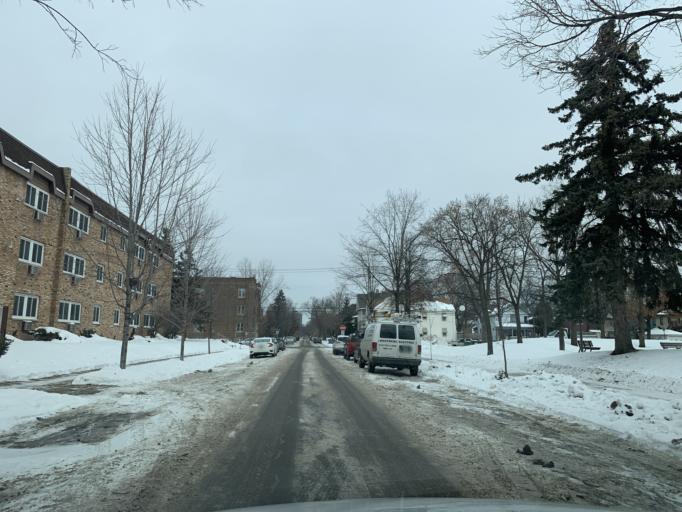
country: US
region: Minnesota
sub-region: Hennepin County
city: Minneapolis
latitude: 44.9548
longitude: -93.2855
